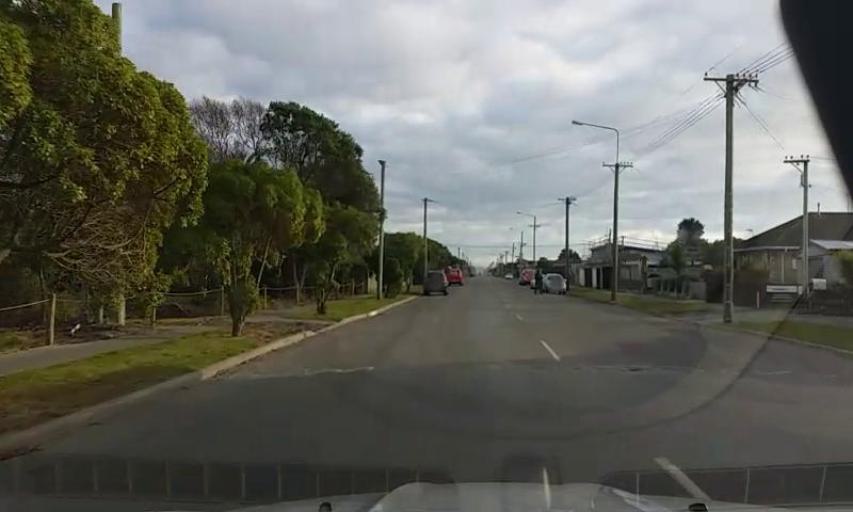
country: NZ
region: Canterbury
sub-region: Christchurch City
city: Christchurch
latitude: -43.5353
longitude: 172.7379
